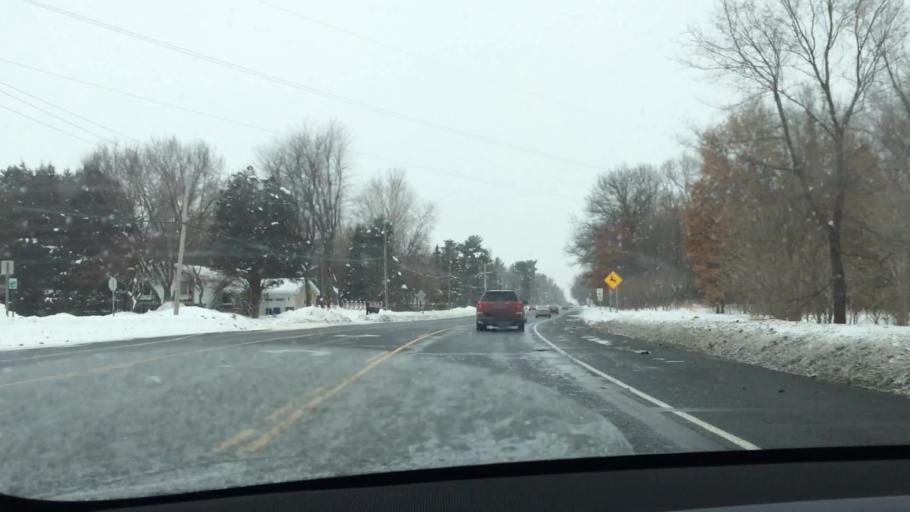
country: US
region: Minnesota
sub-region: Ramsey County
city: Shoreview
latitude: 45.0920
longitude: -93.1270
